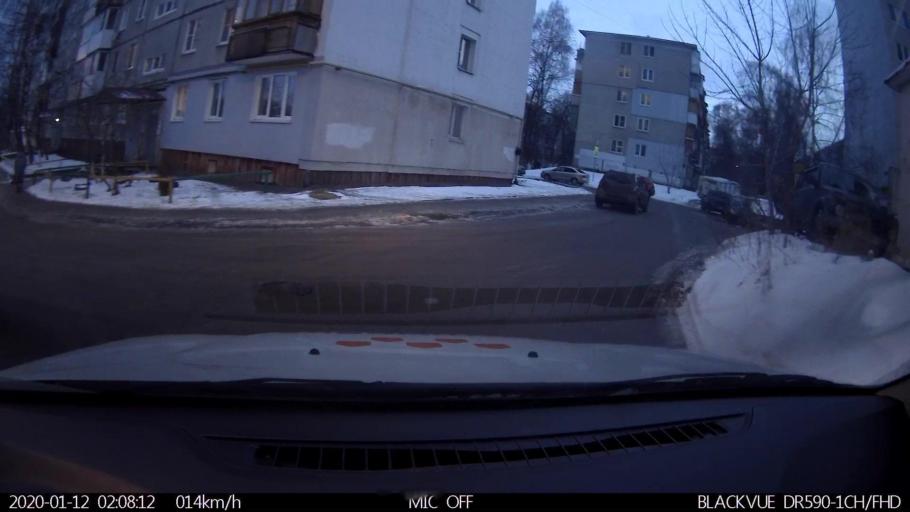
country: RU
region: Nizjnij Novgorod
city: Nizhniy Novgorod
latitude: 56.3049
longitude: 44.0426
